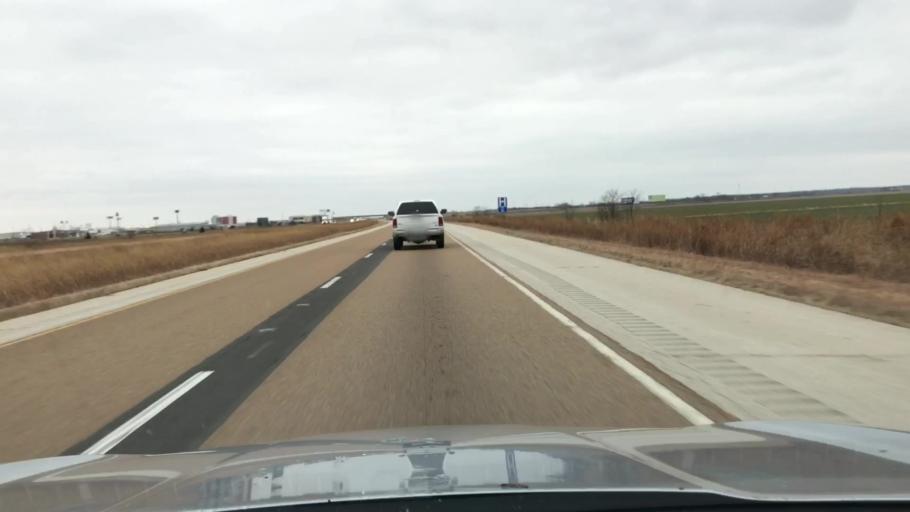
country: US
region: Illinois
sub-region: Montgomery County
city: Litchfield
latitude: 39.1886
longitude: -89.6723
